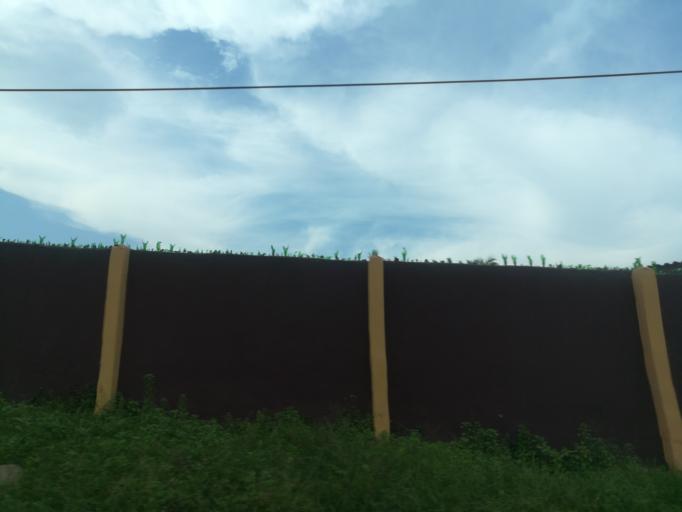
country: NG
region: Oyo
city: Ibadan
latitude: 7.4137
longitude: 3.9045
